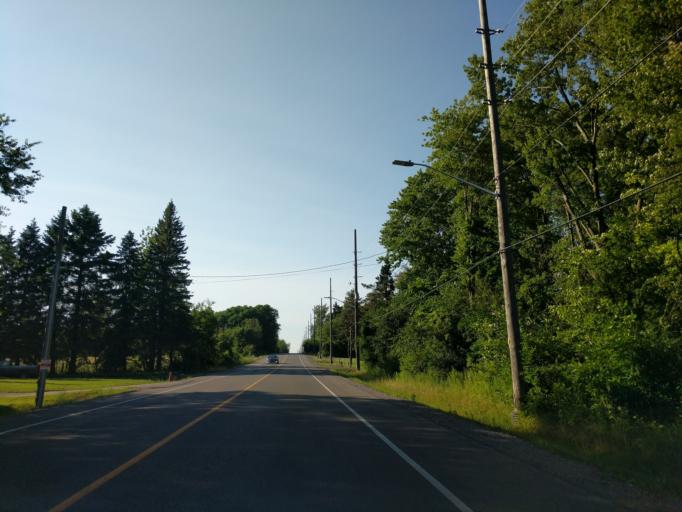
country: CA
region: Ontario
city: Oshawa
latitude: 43.9347
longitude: -78.9118
